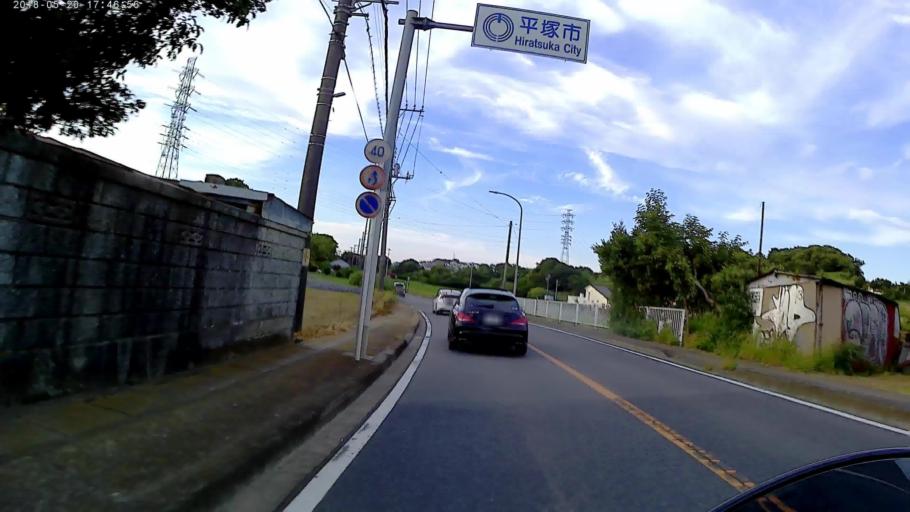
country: JP
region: Kanagawa
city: Oiso
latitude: 35.3307
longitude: 139.2933
